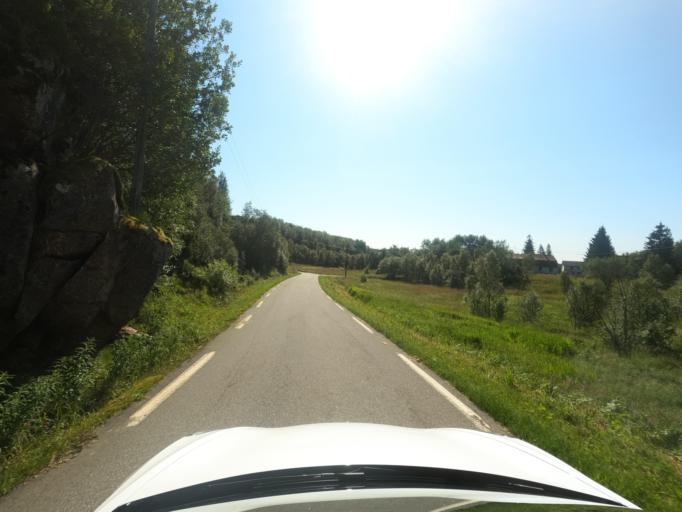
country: NO
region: Nordland
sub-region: Hadsel
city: Stokmarknes
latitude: 68.3039
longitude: 15.0942
